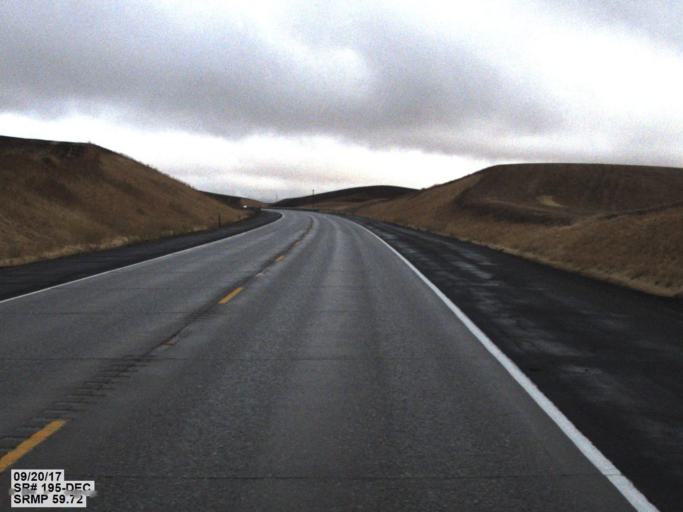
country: US
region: Washington
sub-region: Whitman County
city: Colfax
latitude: 47.1707
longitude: -117.3801
